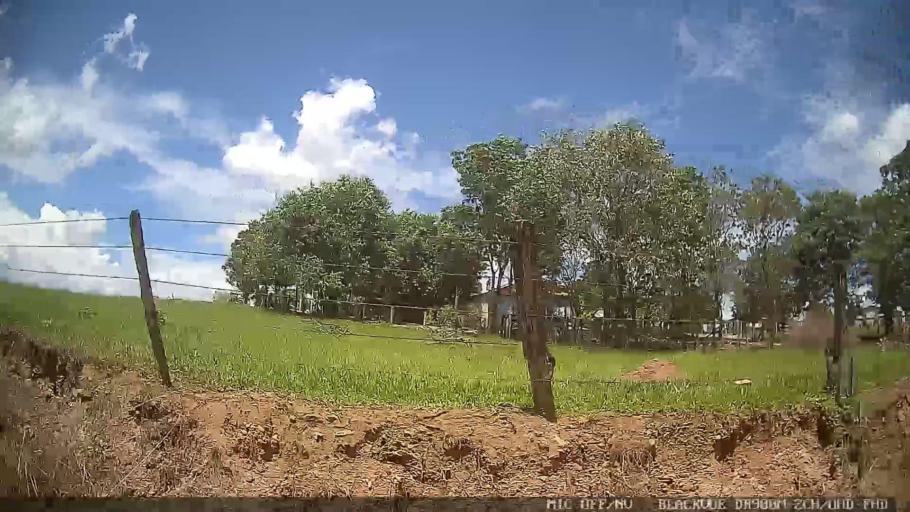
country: BR
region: Sao Paulo
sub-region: Conchas
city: Conchas
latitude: -23.0319
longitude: -47.9956
